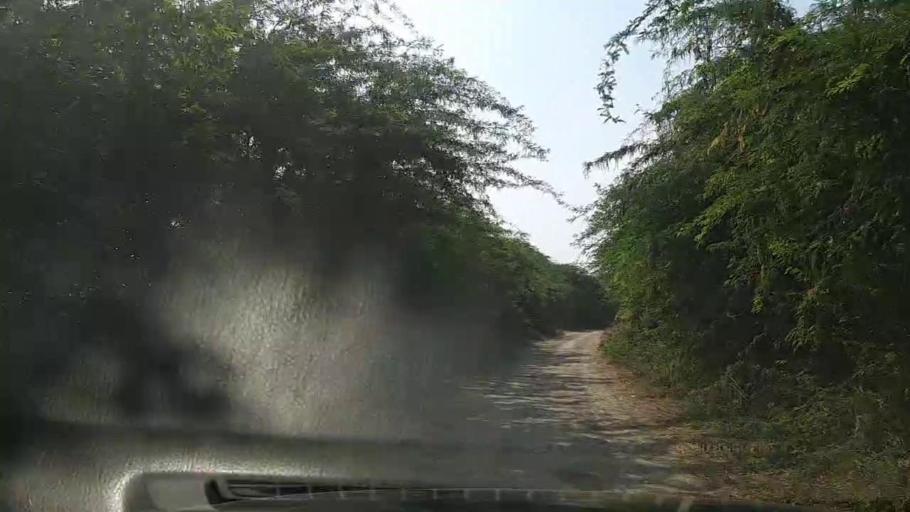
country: PK
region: Sindh
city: Thatta
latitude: 24.7736
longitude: 67.8233
